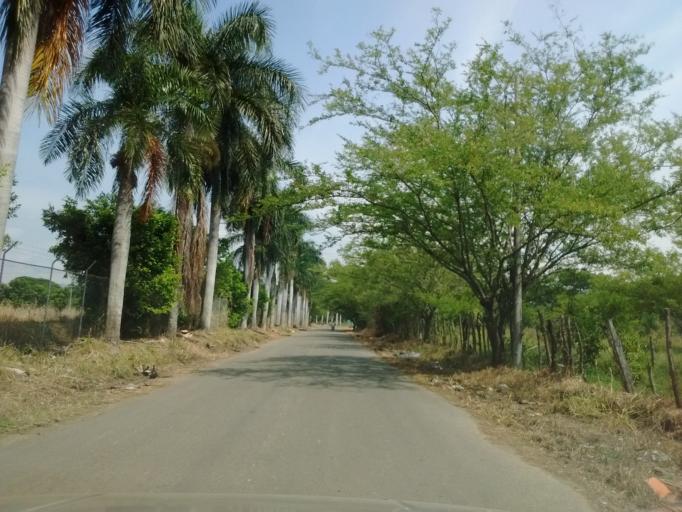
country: CO
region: Cauca
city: Santander de Quilichao
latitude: 3.0243
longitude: -76.4829
